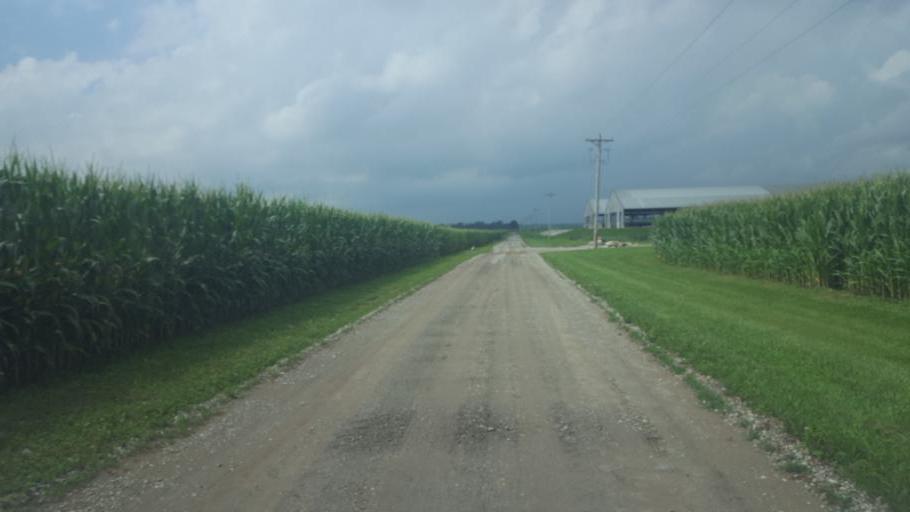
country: US
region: Ohio
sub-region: Union County
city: Richwood
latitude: 40.5297
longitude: -83.3263
